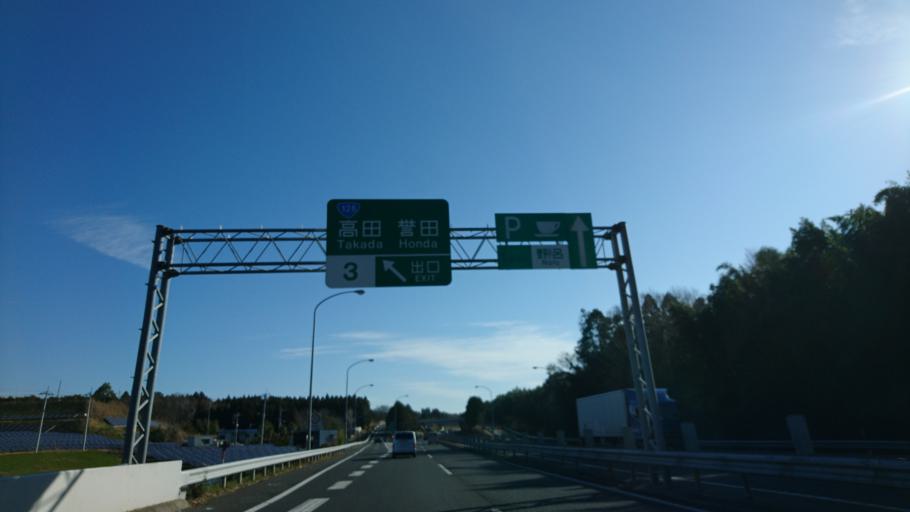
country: JP
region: Chiba
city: Yotsukaido
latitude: 35.5729
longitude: 140.2163
